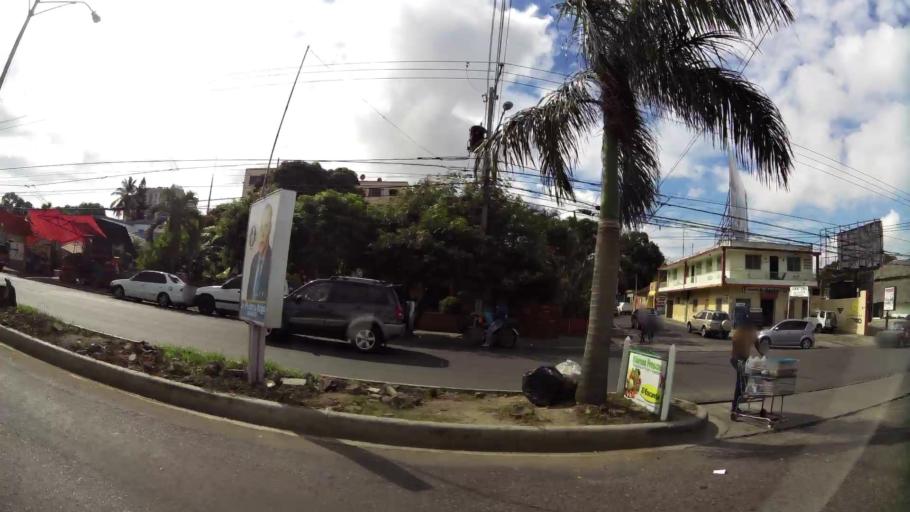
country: DO
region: Santiago
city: Santiago de los Caballeros
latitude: 19.4608
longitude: -70.6824
